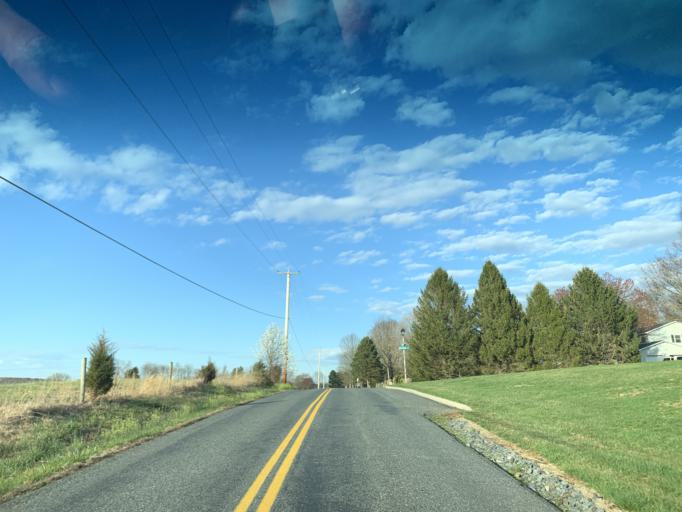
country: US
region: Maryland
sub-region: Harford County
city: South Bel Air
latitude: 39.5935
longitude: -76.2797
